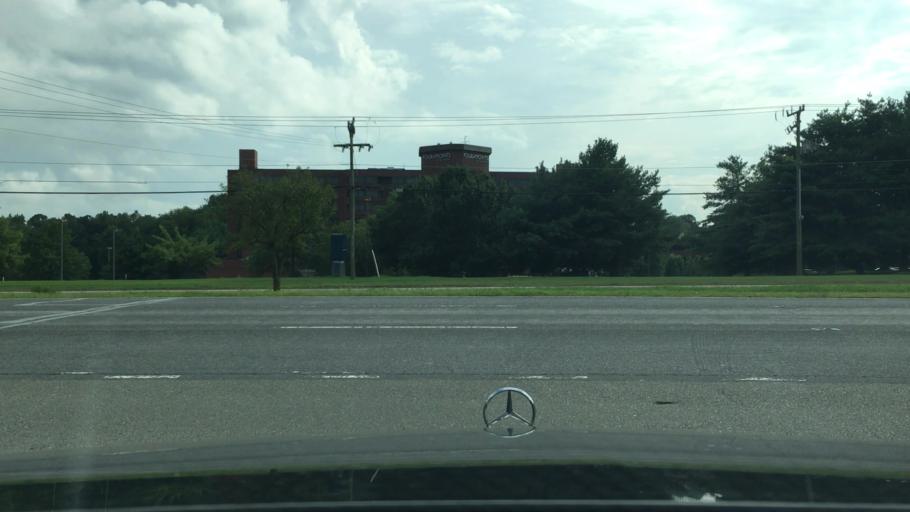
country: US
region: Virginia
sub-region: Chesterfield County
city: Bon Air
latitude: 37.5051
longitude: -77.5781
